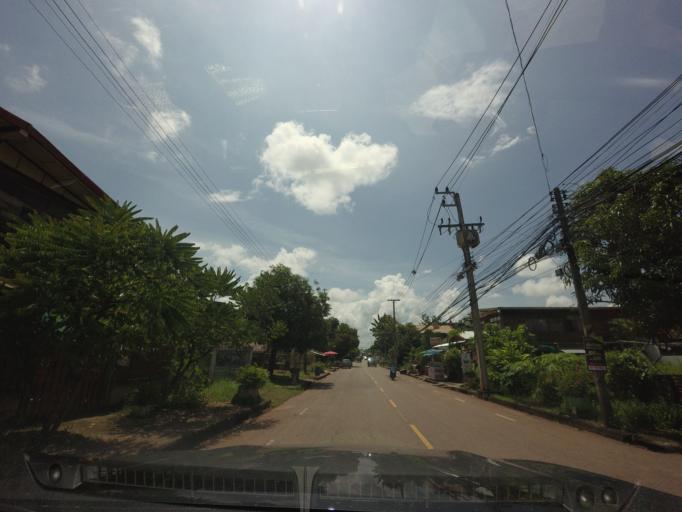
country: TH
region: Changwat Udon Thani
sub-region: Amphoe Ban Phue
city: Ban Phue
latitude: 17.6942
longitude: 102.4662
